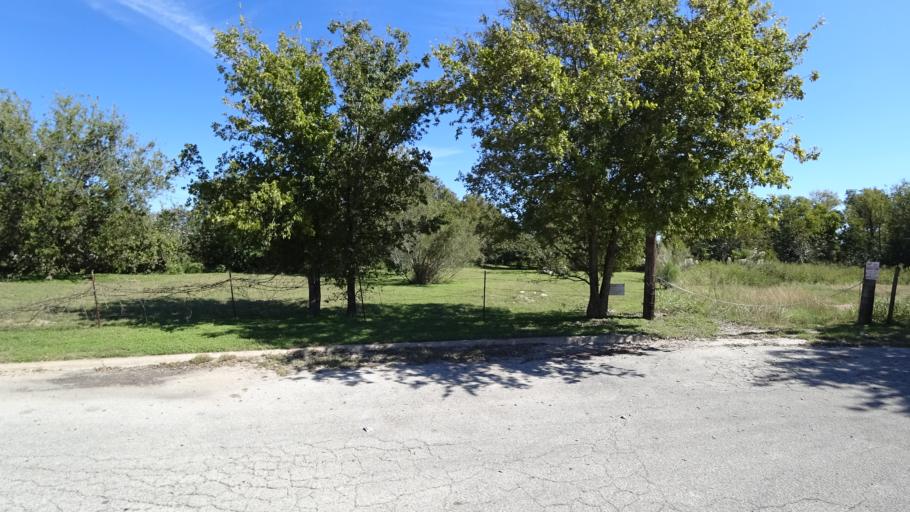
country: US
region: Texas
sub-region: Travis County
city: Austin
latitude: 30.1944
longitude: -97.7079
